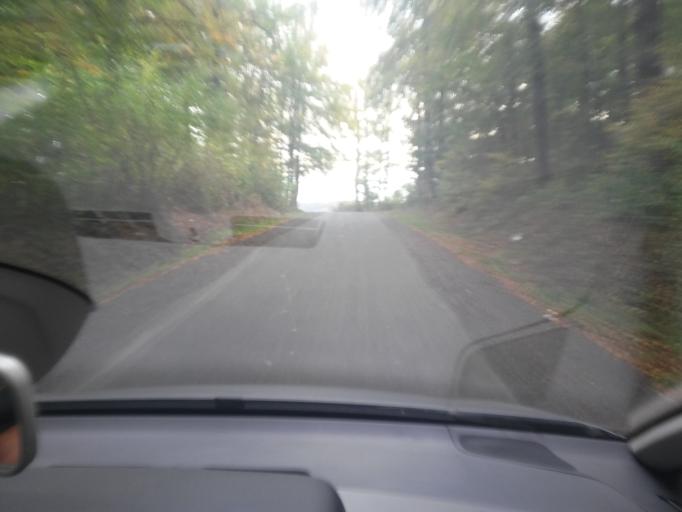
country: BE
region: Wallonia
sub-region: Province du Luxembourg
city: Attert
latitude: 49.7308
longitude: 5.7625
